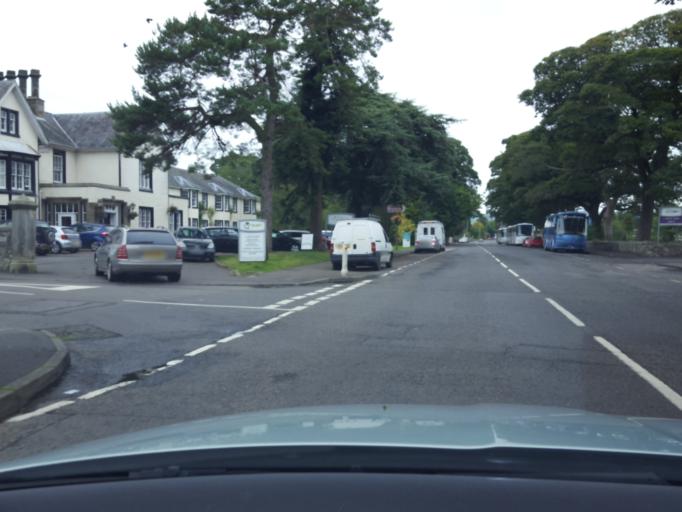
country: GB
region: Scotland
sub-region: Perth and Kinross
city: Kinross
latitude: 56.2081
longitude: -3.4232
